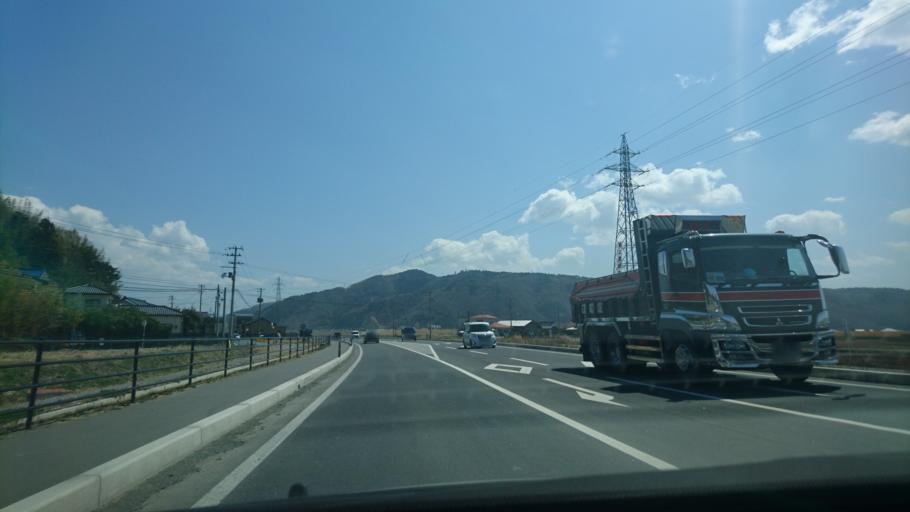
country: JP
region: Miyagi
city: Ishinomaki
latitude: 38.4506
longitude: 141.3170
